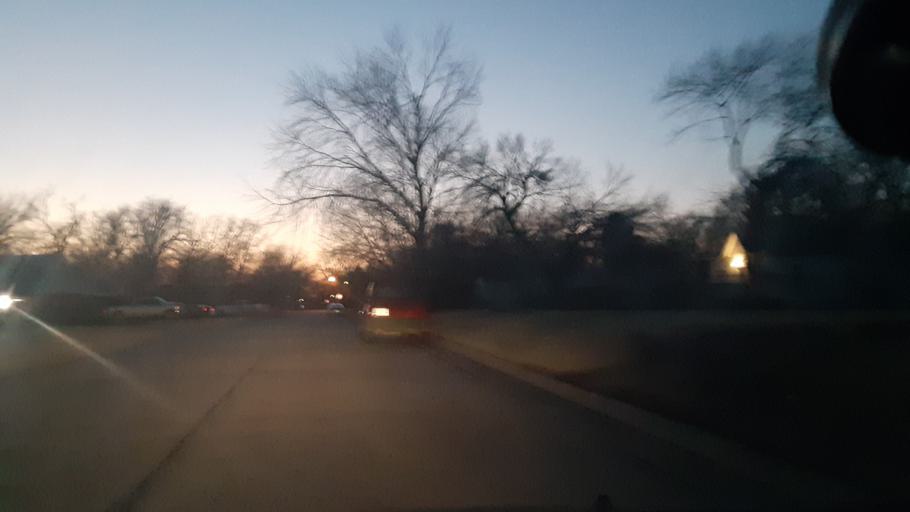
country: US
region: Oklahoma
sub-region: Payne County
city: Stillwater
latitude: 36.1113
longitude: -97.0731
